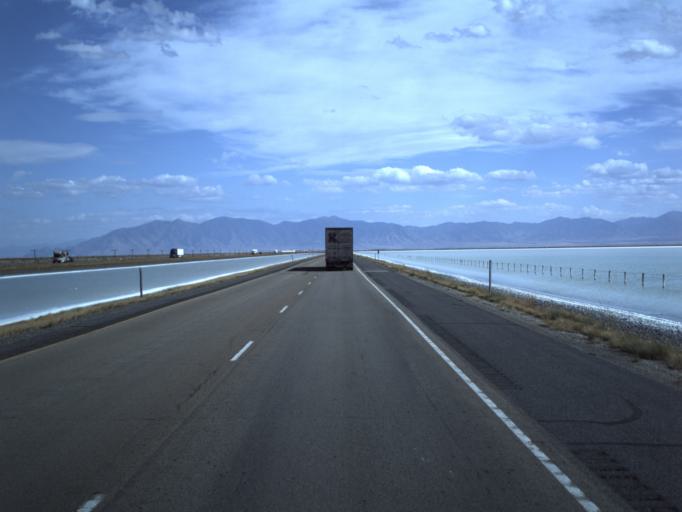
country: US
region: Utah
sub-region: Tooele County
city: Grantsville
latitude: 40.7356
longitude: -112.6087
